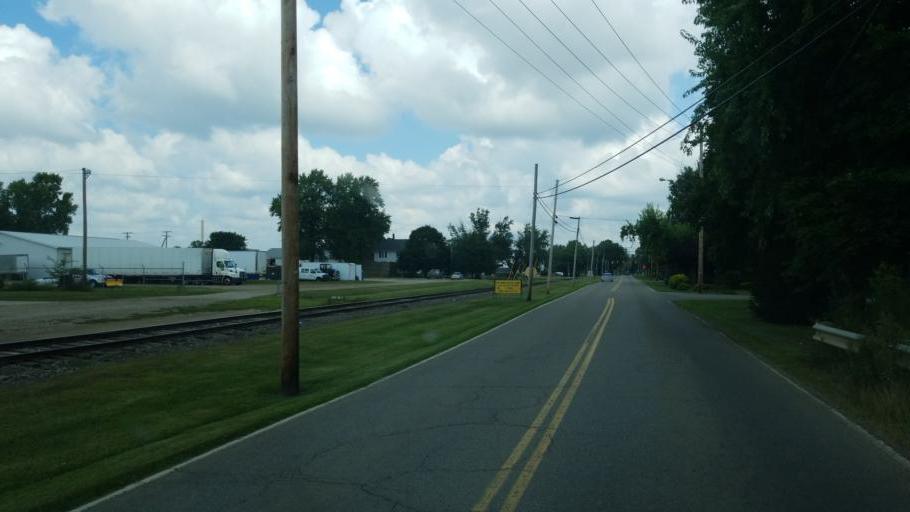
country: US
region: Ohio
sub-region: Knox County
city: Mount Vernon
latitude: 40.3724
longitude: -82.4877
